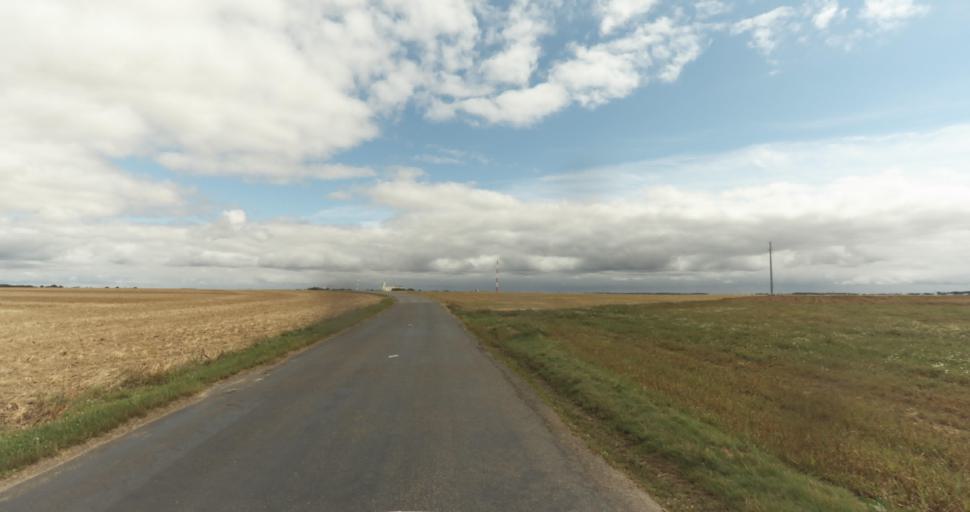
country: FR
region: Haute-Normandie
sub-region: Departement de l'Eure
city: Marcilly-sur-Eure
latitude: 48.9108
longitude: 1.2406
